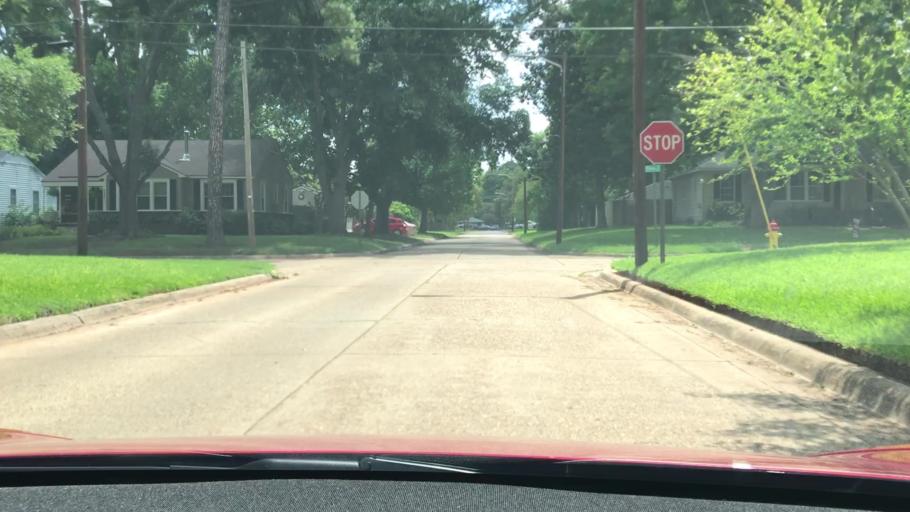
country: US
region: Louisiana
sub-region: Bossier Parish
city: Bossier City
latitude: 32.4579
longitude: -93.7252
